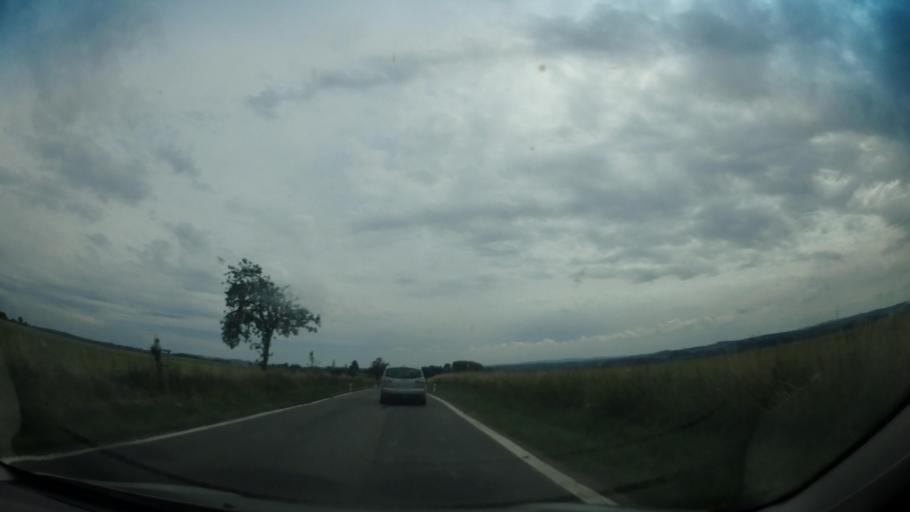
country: CZ
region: Vysocina
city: Bystrice nad Pernstejnem
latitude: 49.5044
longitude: 16.1704
